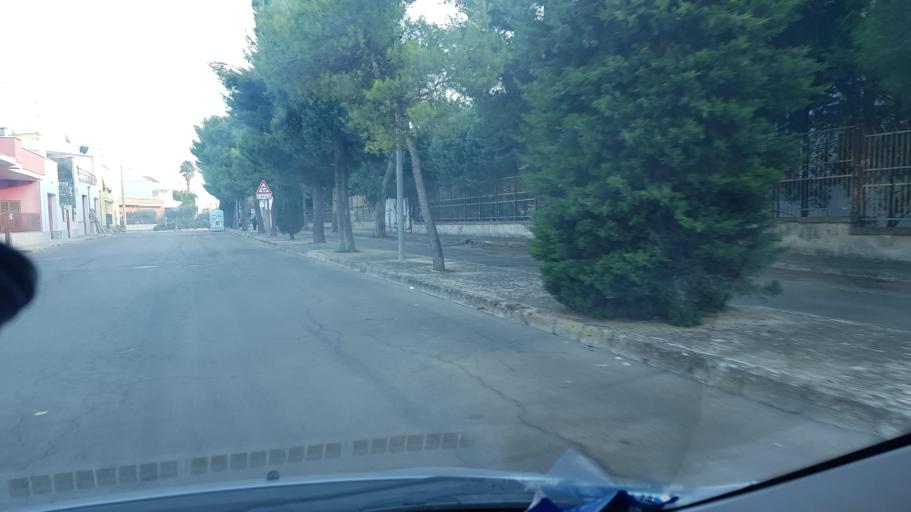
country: IT
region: Apulia
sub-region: Provincia di Lecce
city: Veglie
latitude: 40.3417
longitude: 17.9641
